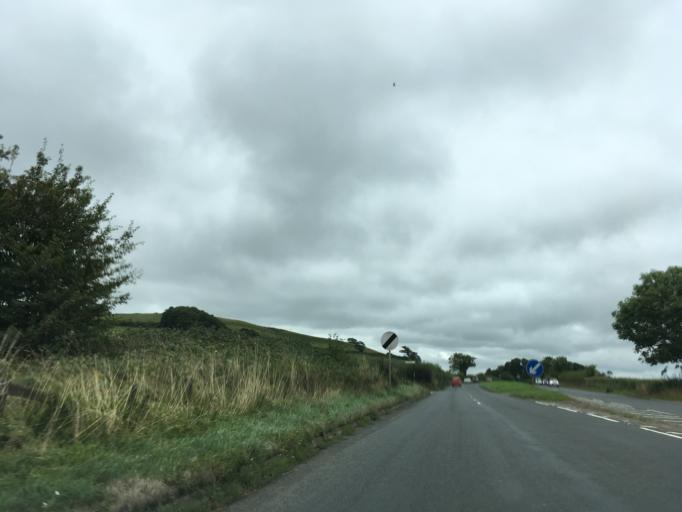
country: GB
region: England
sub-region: Bath and North East Somerset
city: Saltford
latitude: 51.3703
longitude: -2.4779
